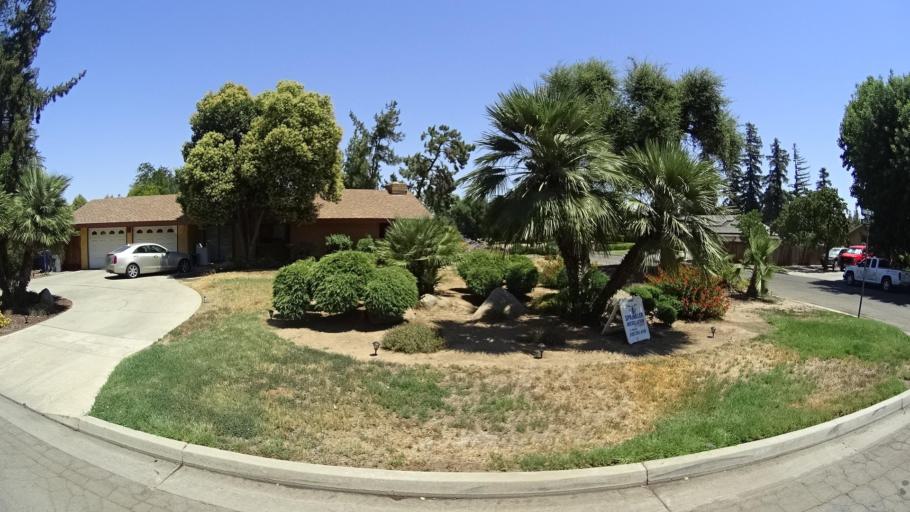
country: US
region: California
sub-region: Fresno County
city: Sunnyside
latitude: 36.7254
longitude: -119.7215
